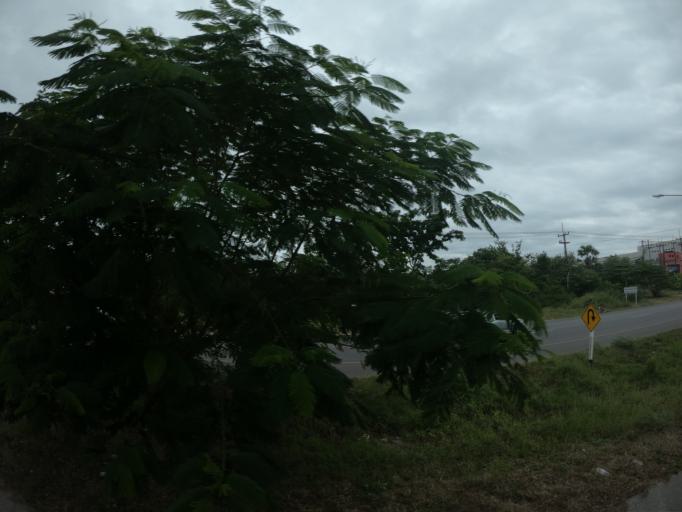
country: TH
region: Maha Sarakham
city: Maha Sarakham
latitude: 16.1622
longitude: 103.3468
